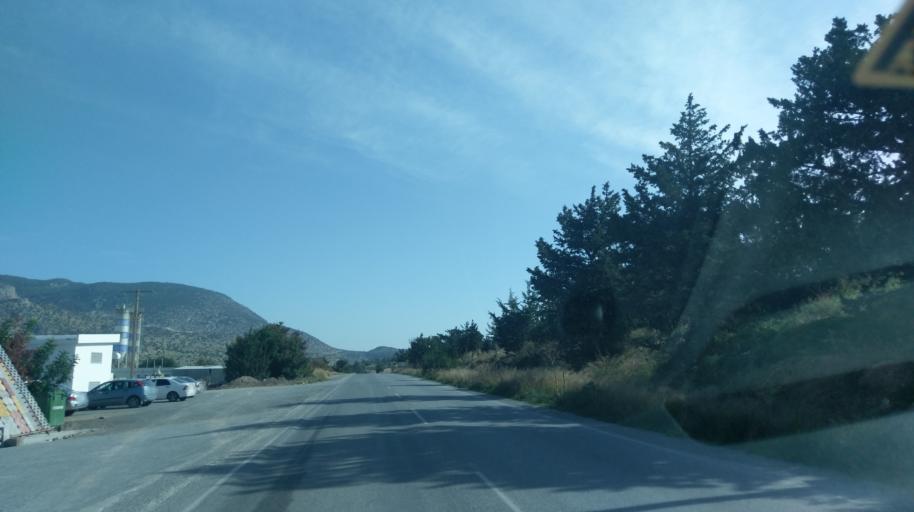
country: CY
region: Lefkosia
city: Nicosia
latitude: 35.2686
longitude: 33.4735
